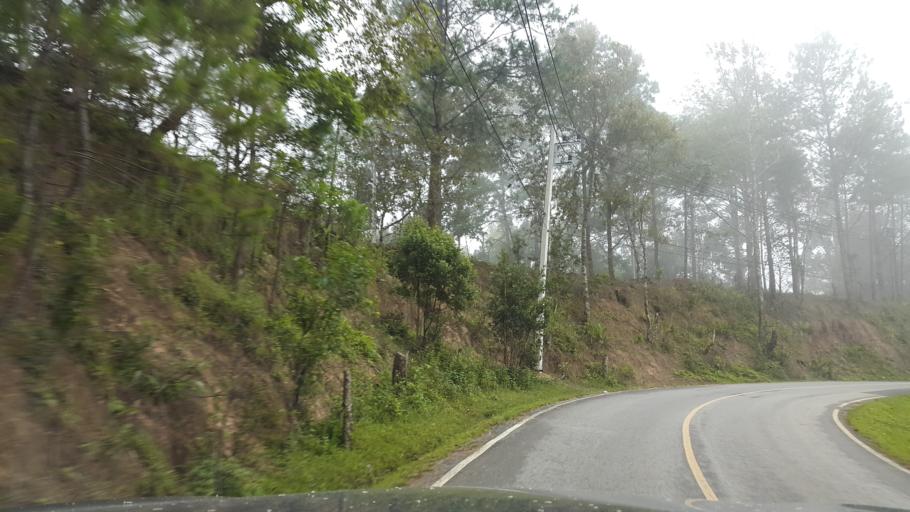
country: TH
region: Chiang Mai
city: Samoeng
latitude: 18.8802
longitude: 98.5248
